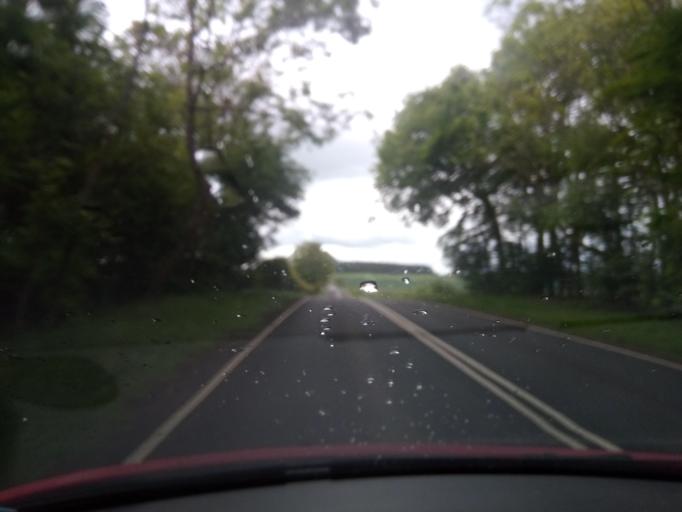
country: GB
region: Scotland
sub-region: The Scottish Borders
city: Saint Boswells
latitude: 55.5444
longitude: -2.6183
